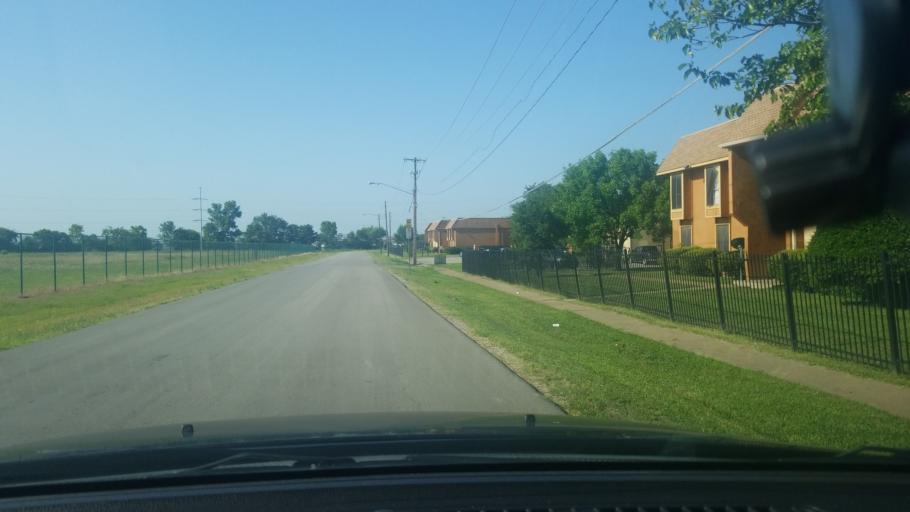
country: US
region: Texas
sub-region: Dallas County
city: Mesquite
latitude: 32.8093
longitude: -96.6654
